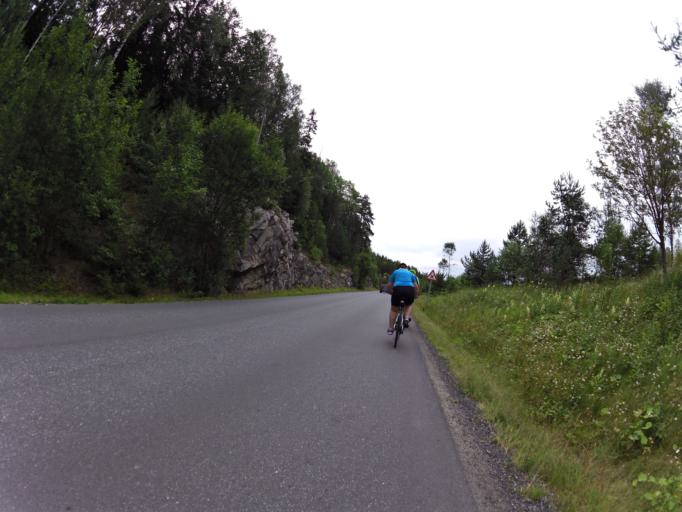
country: NO
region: Akershus
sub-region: As
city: As
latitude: 59.6910
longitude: 10.7347
